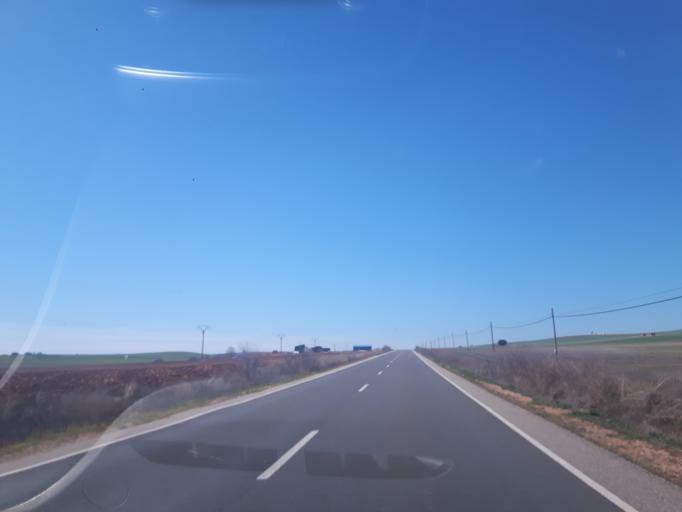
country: ES
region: Castille and Leon
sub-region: Provincia de Salamanca
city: Aldeaseca de Alba
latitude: 40.8443
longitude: -5.4636
